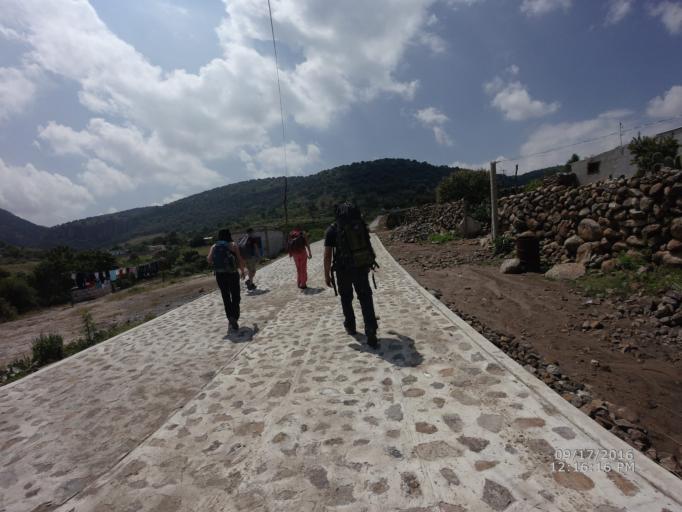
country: MX
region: Queretaro
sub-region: Huimilpan
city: San Jose Tepuzas
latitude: 20.3469
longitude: -100.3742
